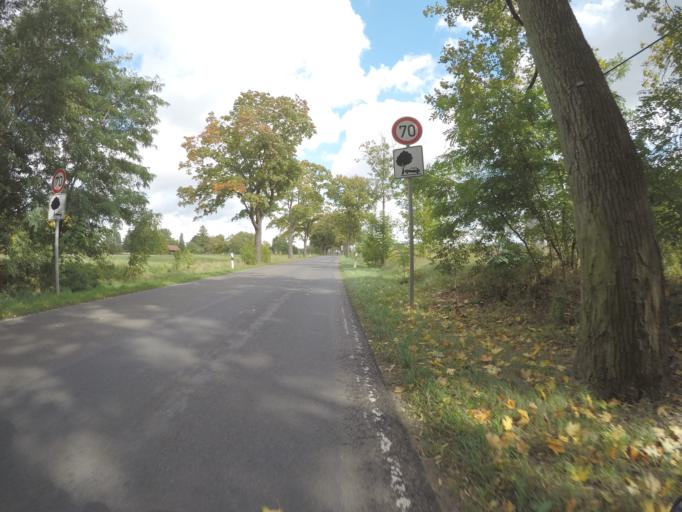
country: DE
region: Brandenburg
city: Altlandsberg
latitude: 52.5724
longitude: 13.7325
